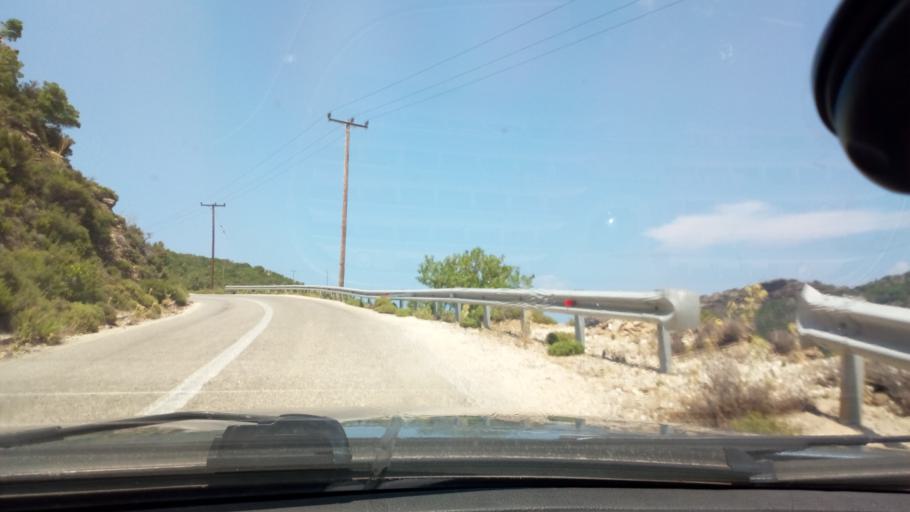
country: GR
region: North Aegean
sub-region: Nomos Samou
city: Agios Kirykos
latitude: 37.6372
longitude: 26.2564
